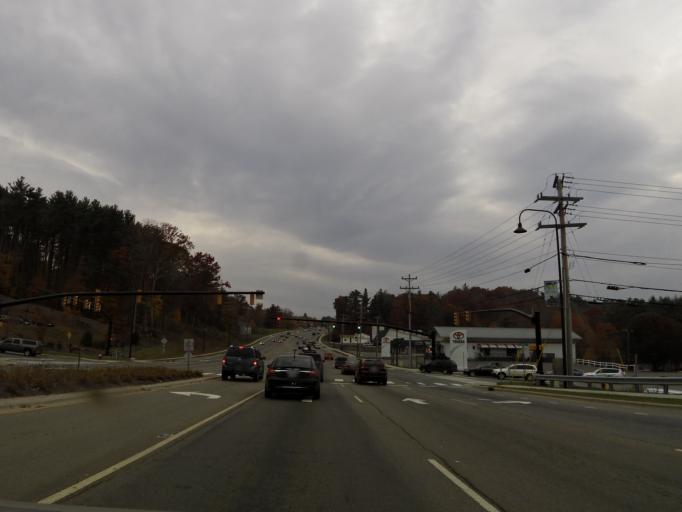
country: US
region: North Carolina
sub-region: Watauga County
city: Boone
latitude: 36.2178
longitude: -81.6632
